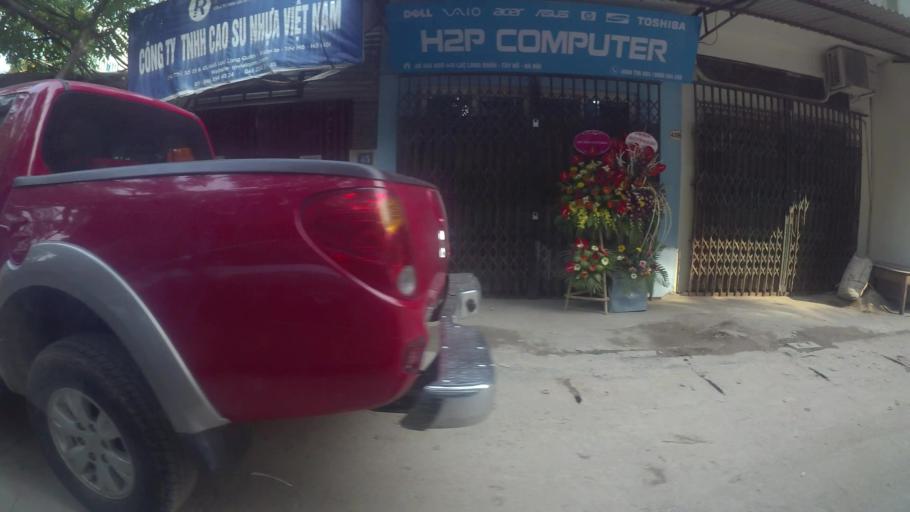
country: VN
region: Ha Noi
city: Tay Ho
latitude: 21.0575
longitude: 105.8065
